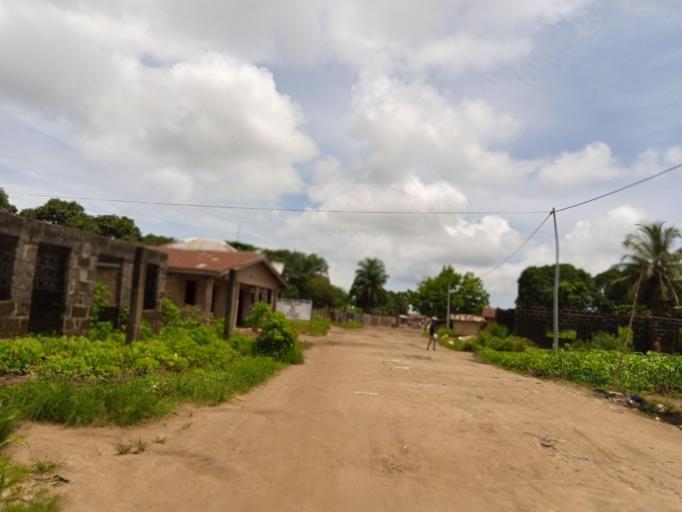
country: SL
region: Northern Province
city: Masoyila
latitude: 8.6029
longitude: -13.1830
